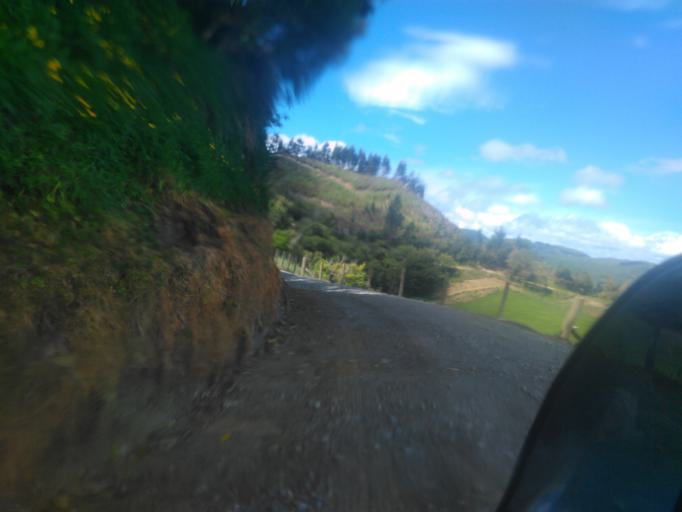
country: NZ
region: Hawke's Bay
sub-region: Wairoa District
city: Wairoa
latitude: -38.7766
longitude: 177.6246
